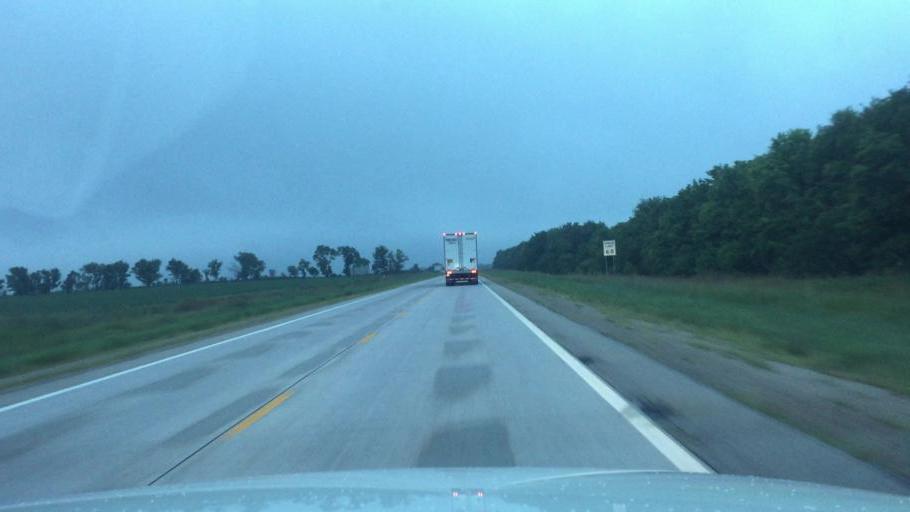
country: US
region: Kansas
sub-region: Neosho County
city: Chanute
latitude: 37.6378
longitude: -95.4797
